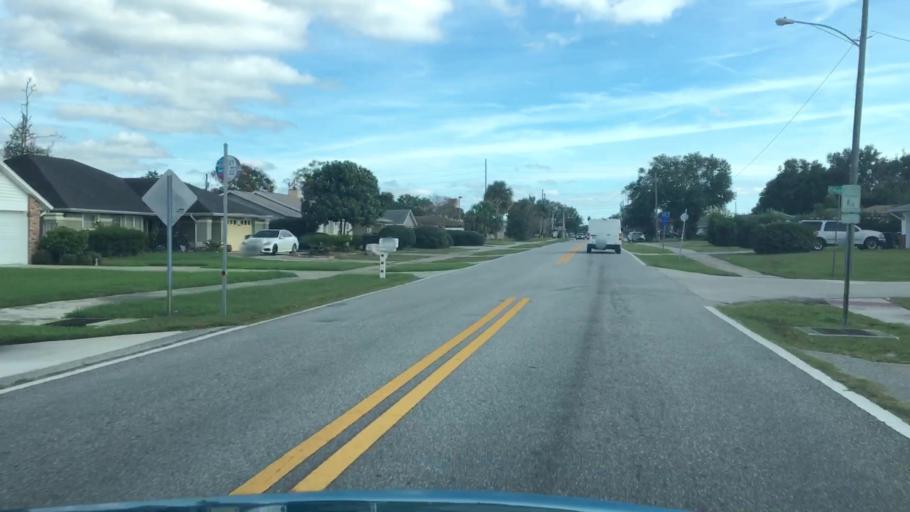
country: US
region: Florida
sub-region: Volusia County
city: Deltona
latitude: 28.8854
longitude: -81.2422
